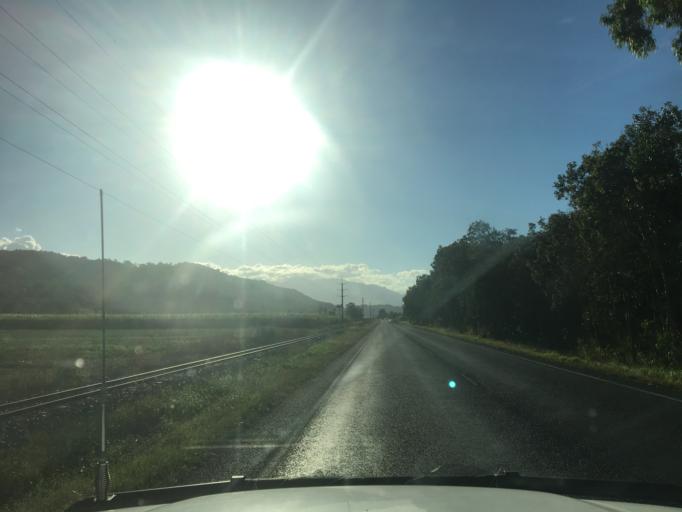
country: AU
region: Queensland
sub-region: Cairns
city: Port Douglas
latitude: -16.4998
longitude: 145.4311
